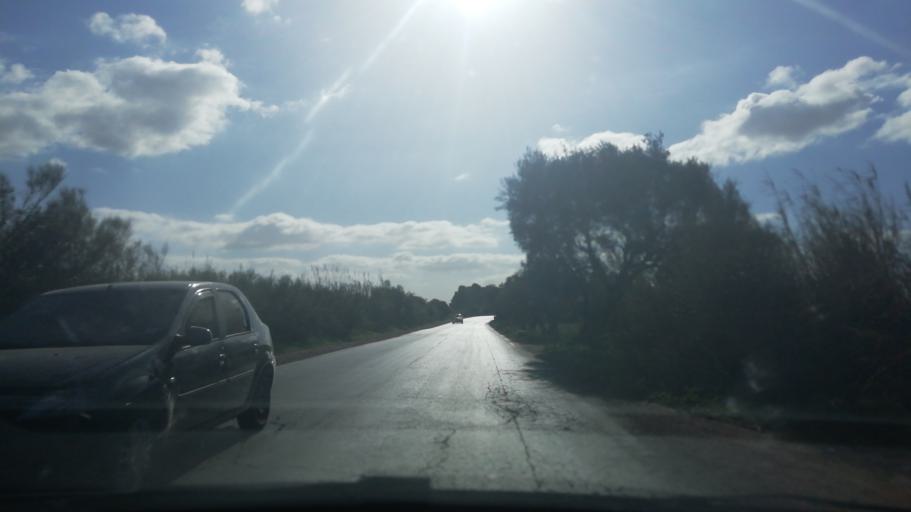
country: DZ
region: Mostaganem
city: Mostaganem
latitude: 35.9565
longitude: 0.2462
